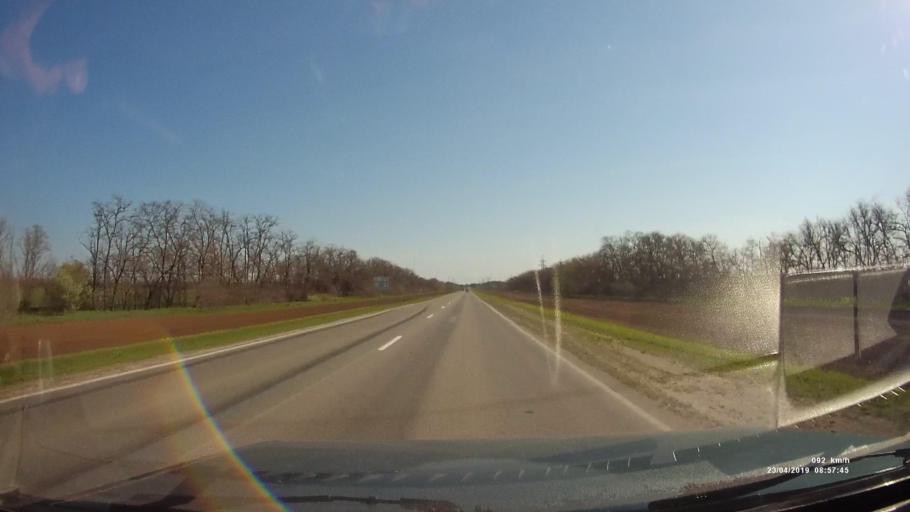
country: RU
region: Rostov
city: Sal'sk
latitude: 46.5038
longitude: 41.5277
